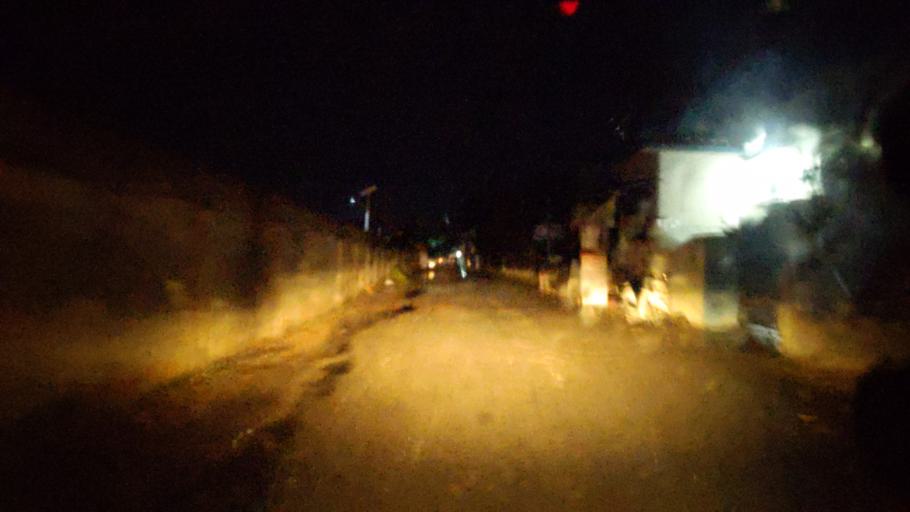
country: IN
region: Uttarakhand
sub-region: Naini Tal
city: Haldwani
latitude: 29.2070
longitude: 79.5023
